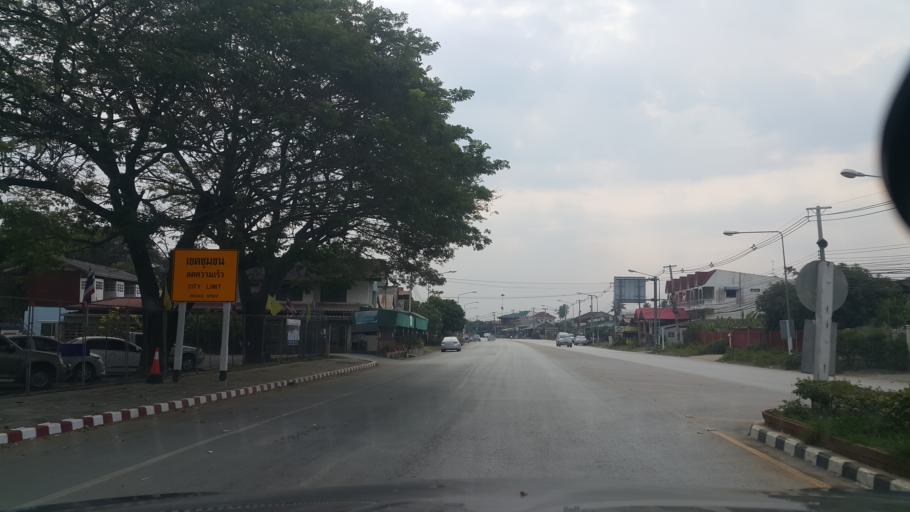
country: TH
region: Sukhothai
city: Si Samrong
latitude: 17.1625
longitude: 99.8626
